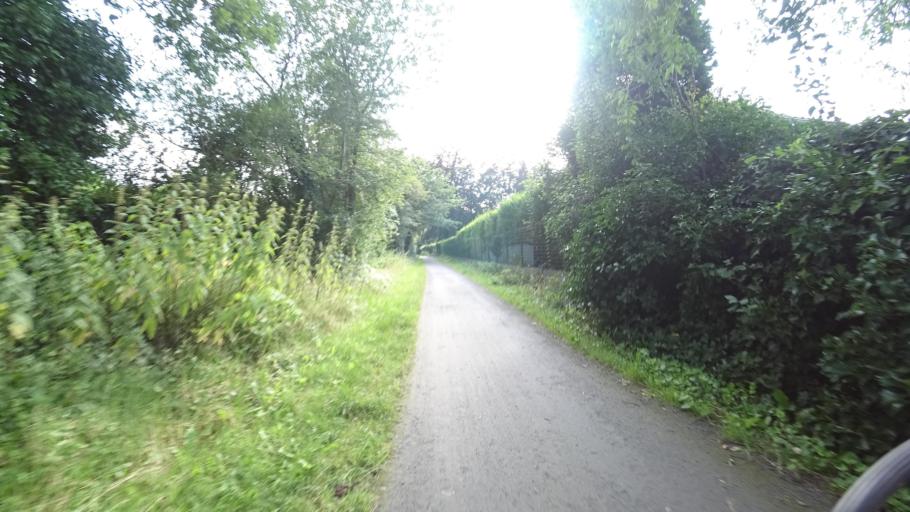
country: BE
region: Flanders
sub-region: Provincie West-Vlaanderen
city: Sint-Kruis
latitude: 51.1979
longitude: 3.2739
